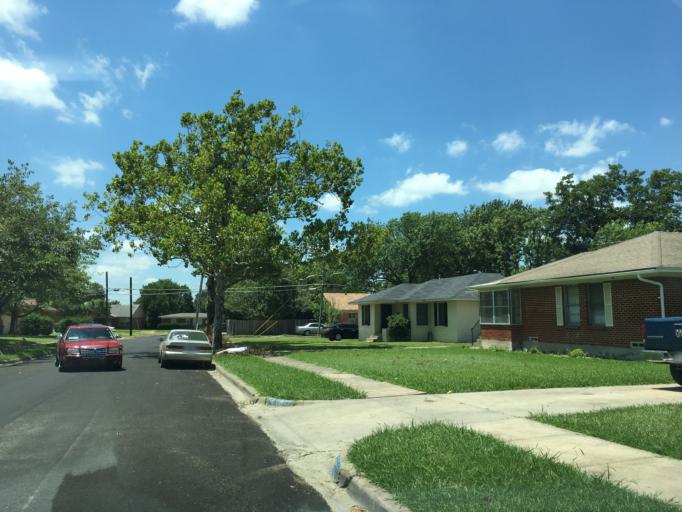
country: US
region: Texas
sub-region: Dallas County
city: Garland
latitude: 32.8367
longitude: -96.6700
